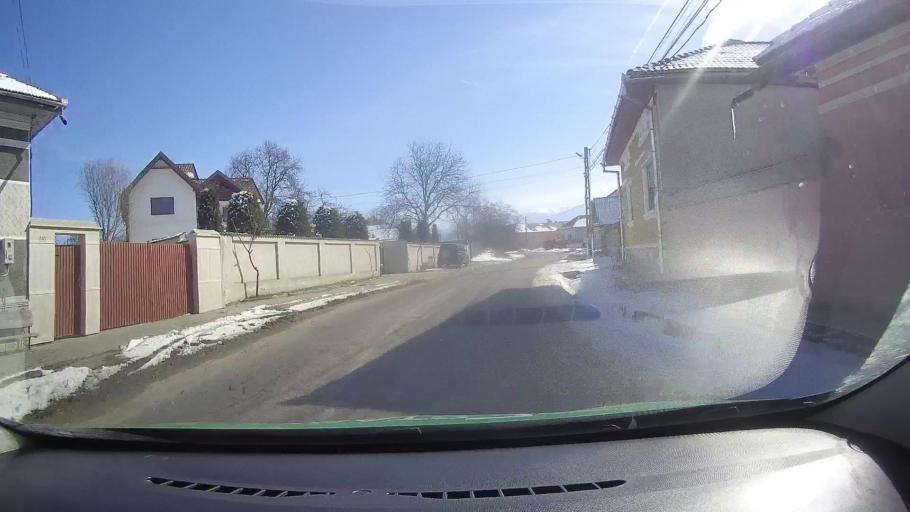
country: RO
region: Brasov
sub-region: Comuna Lisa
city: Lisa
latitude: 45.7246
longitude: 24.8529
